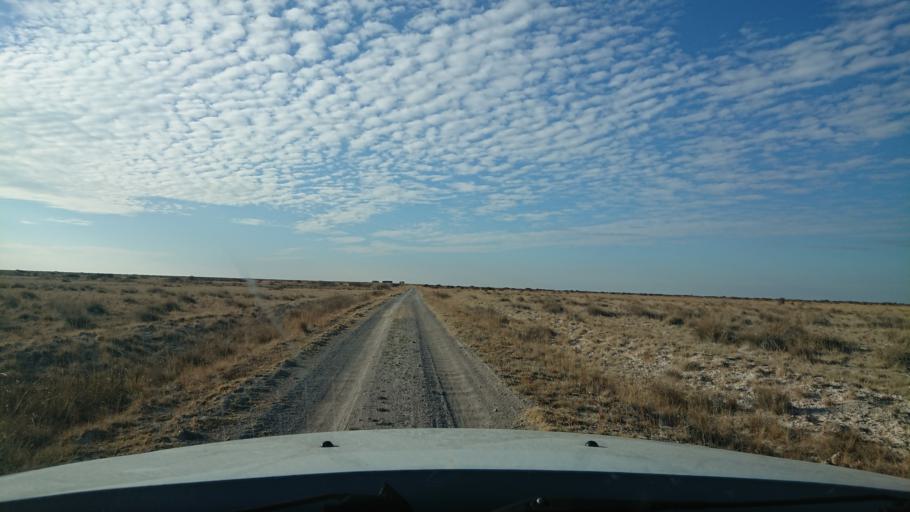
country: TR
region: Aksaray
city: Eskil
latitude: 38.5435
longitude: 33.3281
